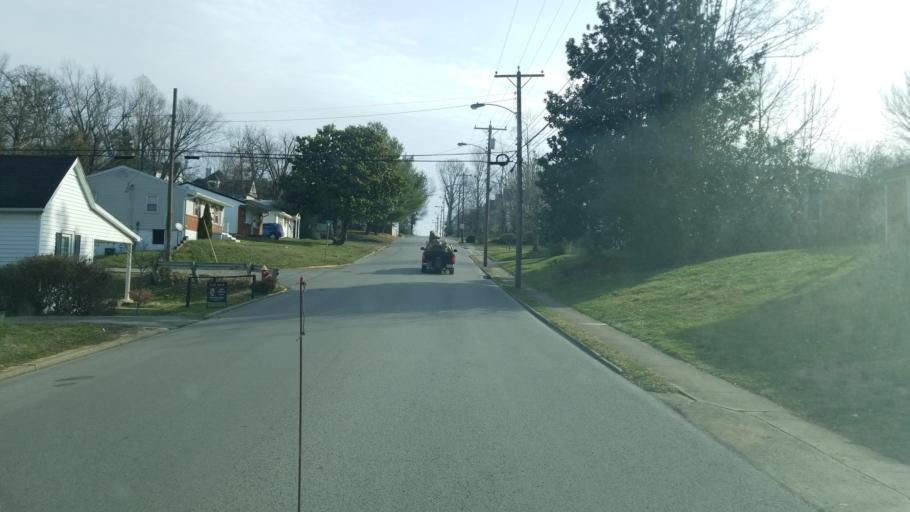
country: US
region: Kentucky
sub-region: Boyle County
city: Danville
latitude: 37.6494
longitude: -84.7784
